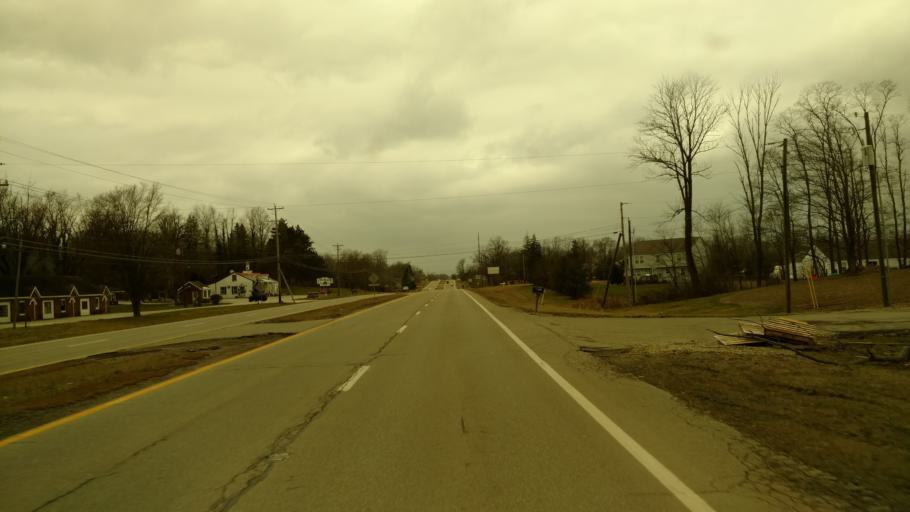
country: US
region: Ohio
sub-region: Licking County
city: Etna
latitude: 39.9580
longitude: -82.6485
